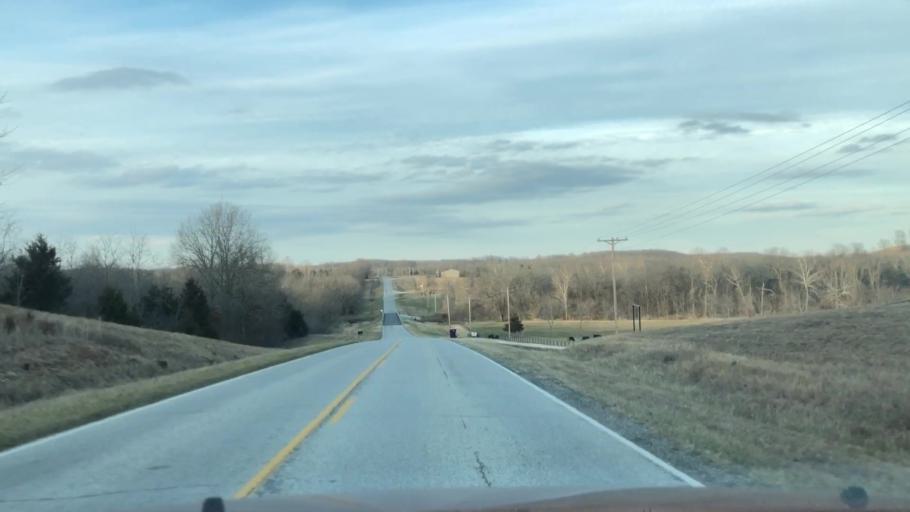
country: US
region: Missouri
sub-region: Webster County
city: Marshfield
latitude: 37.2432
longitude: -92.8798
